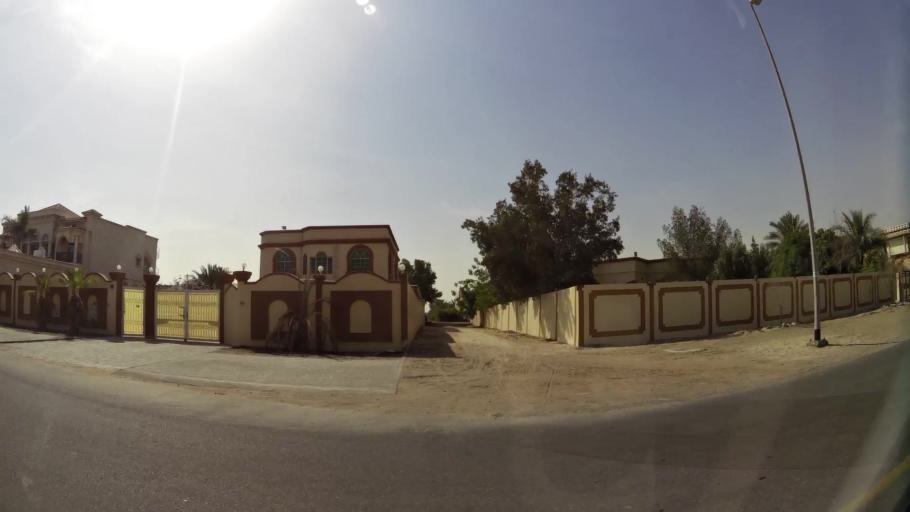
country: AE
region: Ash Shariqah
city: Sharjah
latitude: 25.2724
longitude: 55.4017
